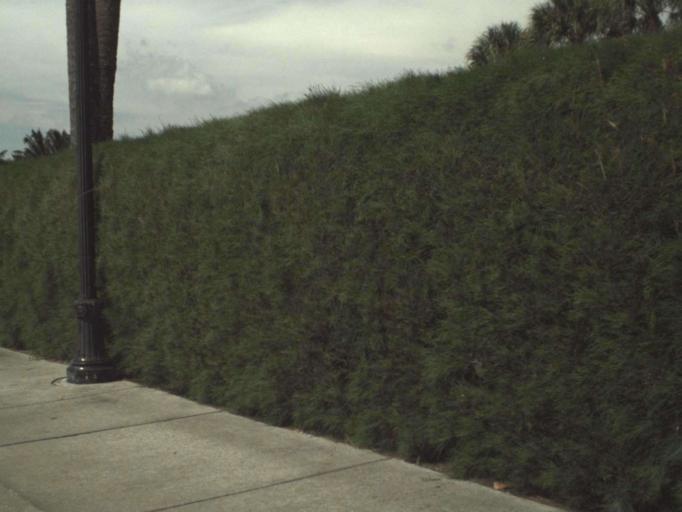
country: US
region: Florida
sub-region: Palm Beach County
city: Palm Beach
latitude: 26.7137
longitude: -80.0378
